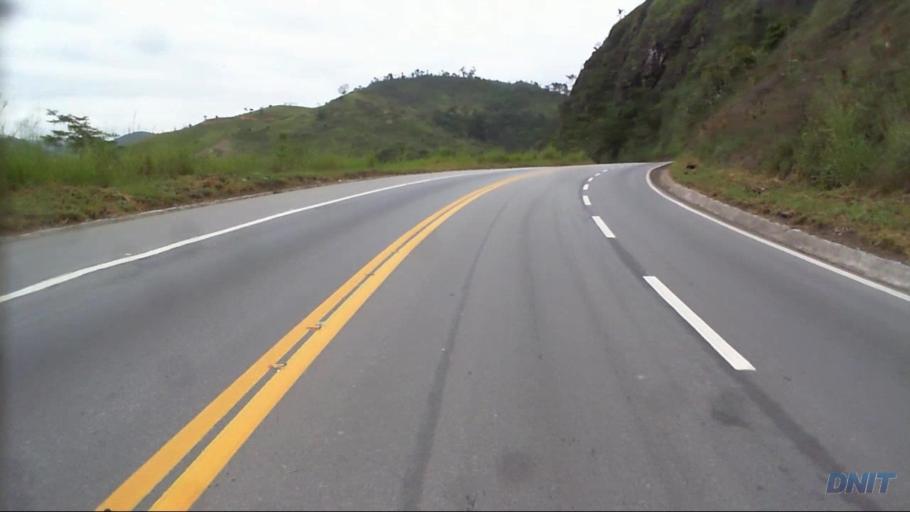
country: BR
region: Minas Gerais
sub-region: Timoteo
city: Timoteo
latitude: -19.6392
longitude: -42.8137
